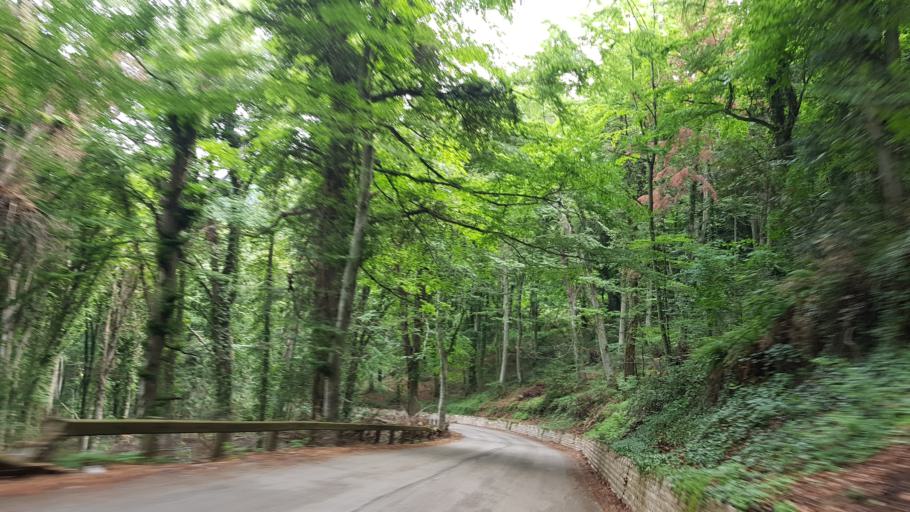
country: IT
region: Basilicate
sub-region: Provincia di Potenza
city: Rionero in Vulture
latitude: 40.9257
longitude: 15.6105
